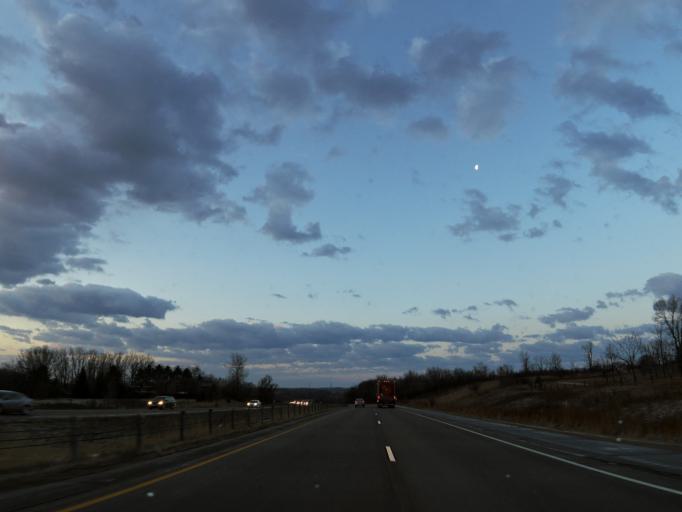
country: US
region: Minnesota
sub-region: Dakota County
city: Lakeville
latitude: 44.6206
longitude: -93.2983
